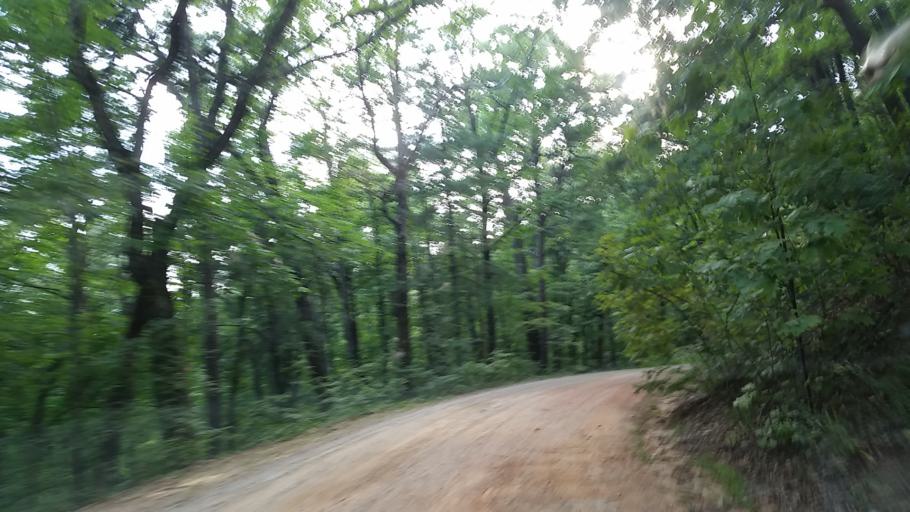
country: US
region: Georgia
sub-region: Lumpkin County
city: Dahlonega
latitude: 34.6394
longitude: -84.0956
